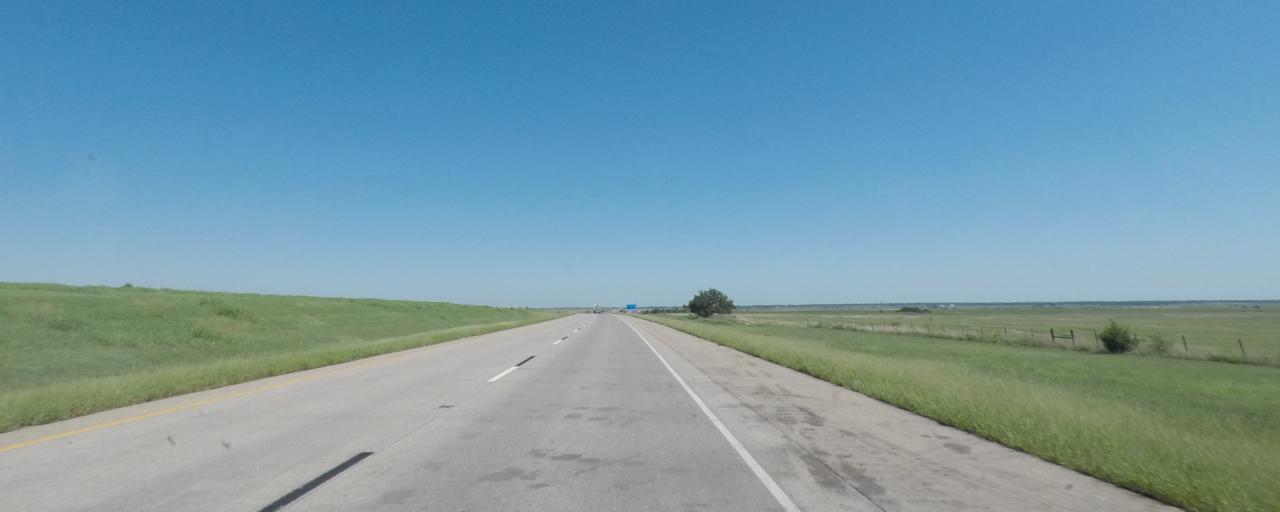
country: US
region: Oklahoma
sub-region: Kay County
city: Tonkawa
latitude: 36.5941
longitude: -97.3453
